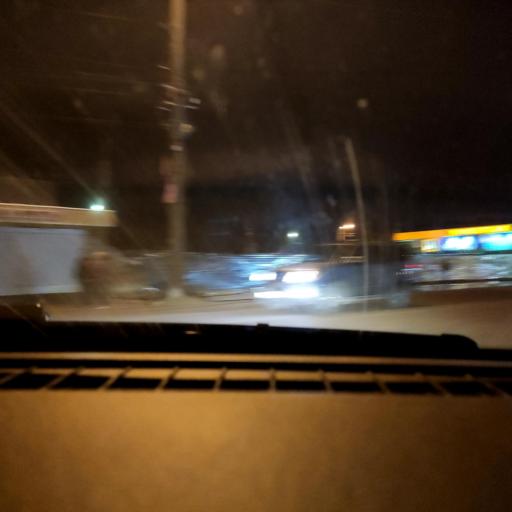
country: RU
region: Voronezj
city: Maslovka
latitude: 51.6349
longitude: 39.2737
